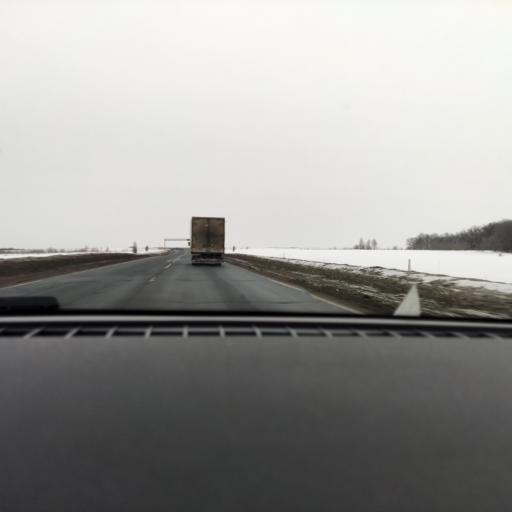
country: RU
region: Samara
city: Petra-Dubrava
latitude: 53.3320
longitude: 50.4537
